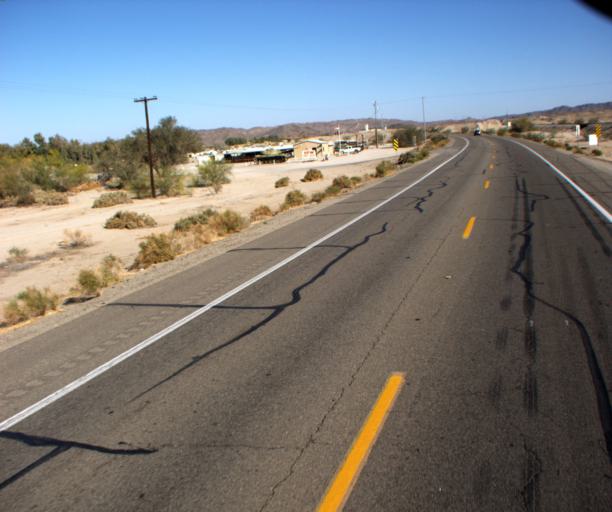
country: US
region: Arizona
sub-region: Yuma County
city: Fortuna Foothills
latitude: 32.7267
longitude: -114.4212
